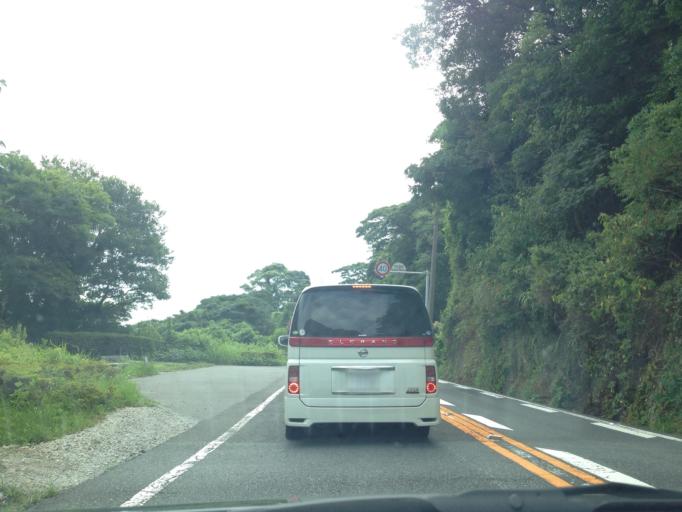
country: JP
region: Shizuoka
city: Shimoda
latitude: 34.7269
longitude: 138.9901
